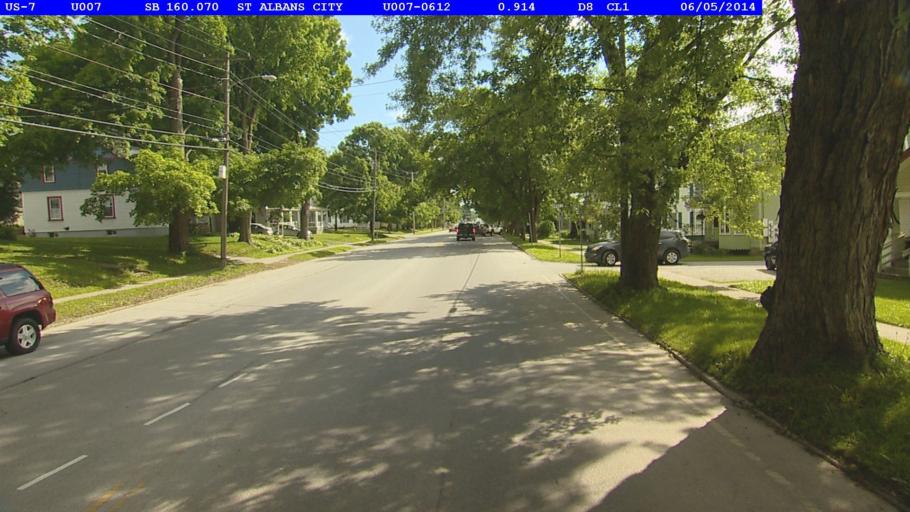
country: US
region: Vermont
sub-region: Franklin County
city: Saint Albans
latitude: 44.8062
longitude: -73.0851
